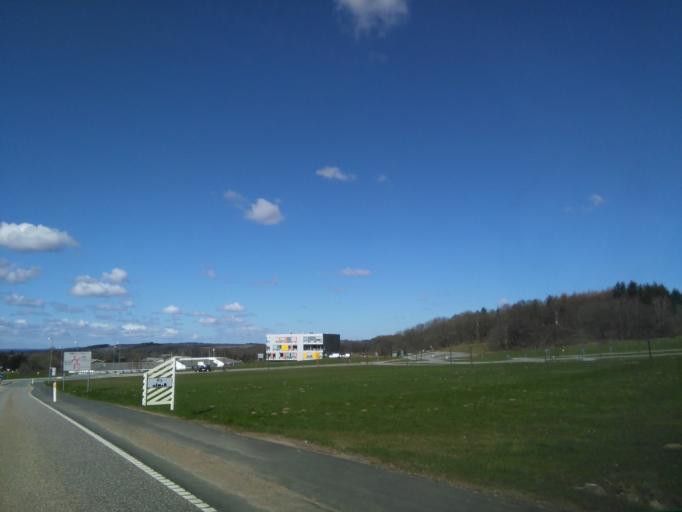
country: DK
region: Central Jutland
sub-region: Skanderborg Kommune
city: Ry
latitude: 56.0892
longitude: 9.7869
